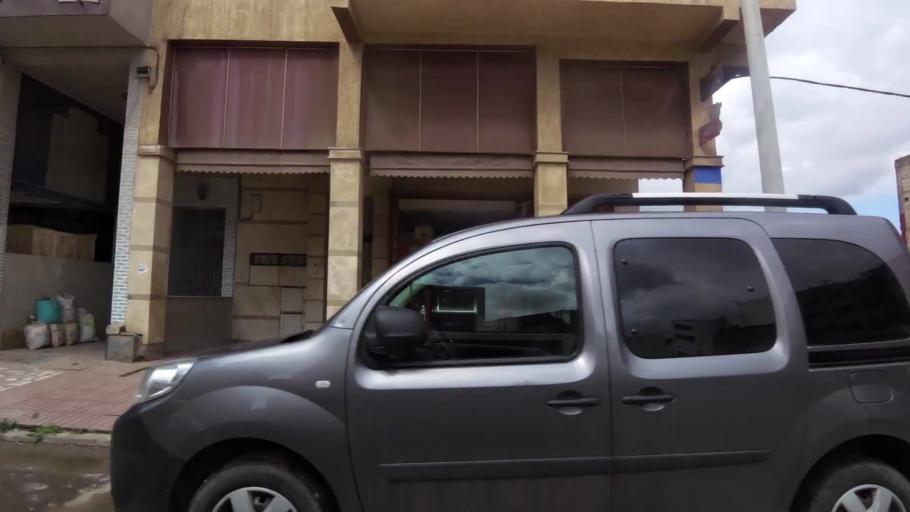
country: MA
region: Grand Casablanca
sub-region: Nouaceur
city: Bouskoura
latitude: 33.5190
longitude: -7.6515
